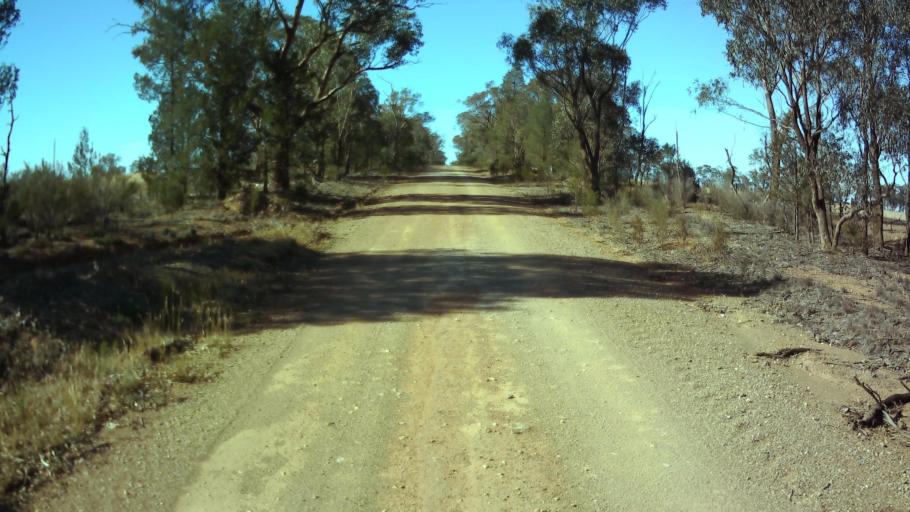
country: AU
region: New South Wales
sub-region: Weddin
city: Grenfell
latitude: -33.8981
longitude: 147.8791
